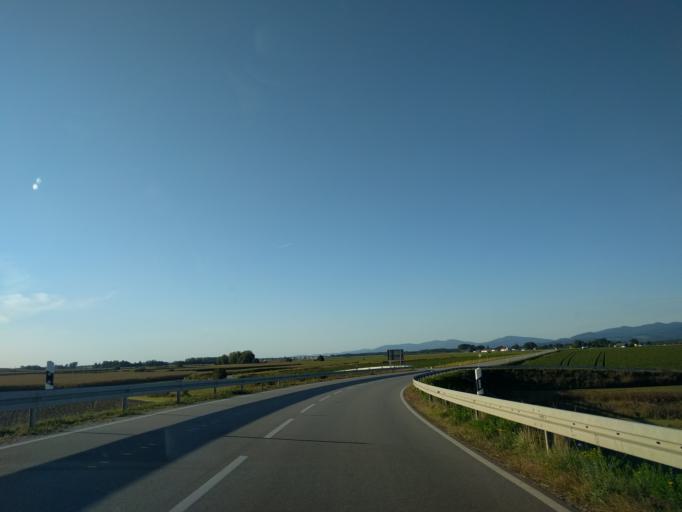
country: DE
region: Bavaria
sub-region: Lower Bavaria
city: Osterhofen
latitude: 48.7033
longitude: 13.0036
